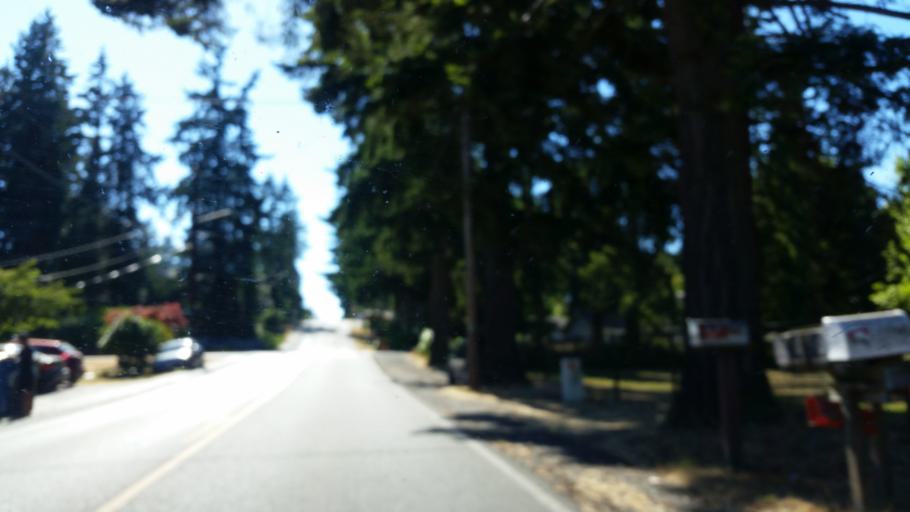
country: US
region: Washington
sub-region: Snohomish County
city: Esperance
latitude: 47.7961
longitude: -122.3403
